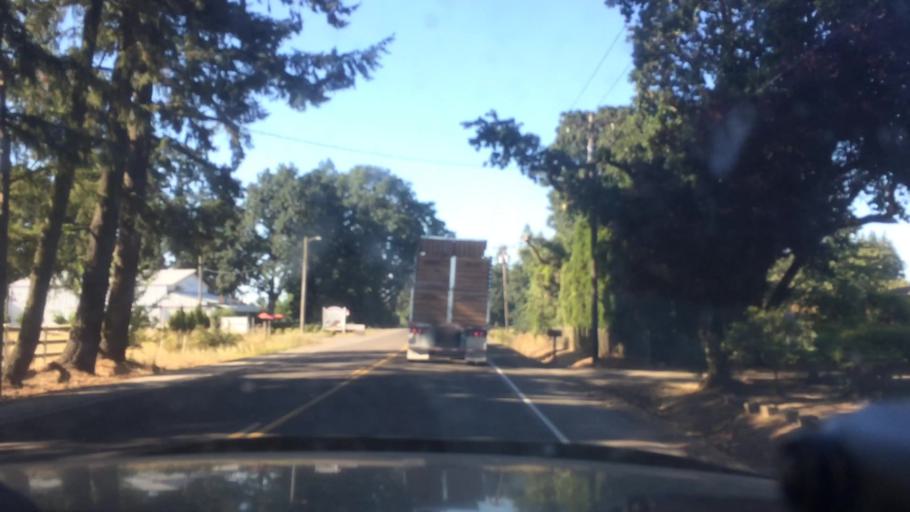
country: US
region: Oregon
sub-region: Marion County
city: Hayesville
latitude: 45.0689
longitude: -122.9798
